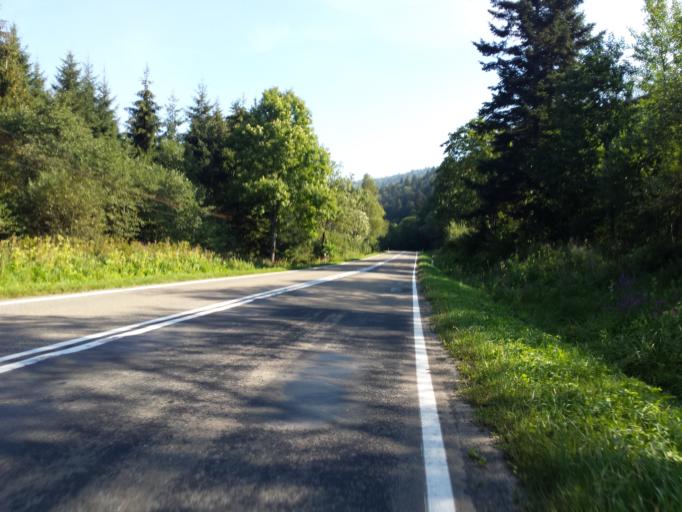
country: PL
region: Subcarpathian Voivodeship
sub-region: Powiat leski
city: Baligrod
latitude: 49.2994
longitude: 22.2728
